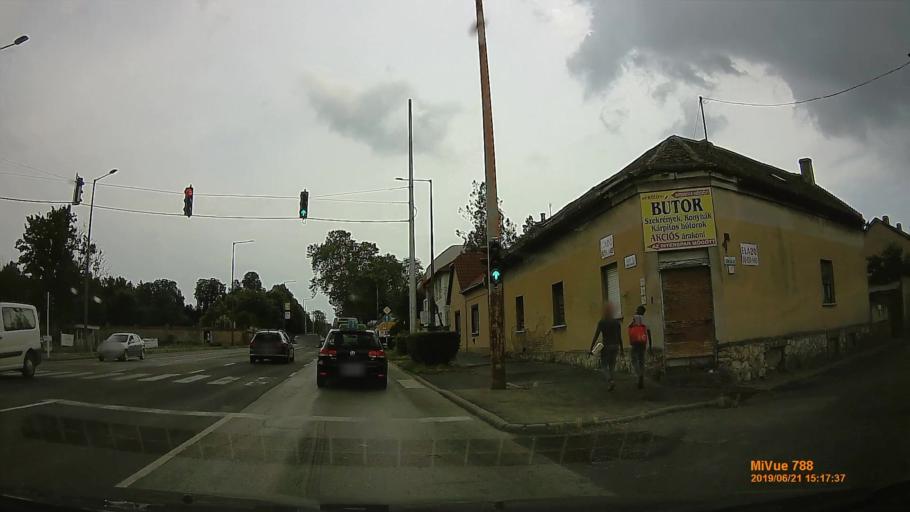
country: HU
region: Baranya
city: Pecs
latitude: 46.0560
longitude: 18.2308
